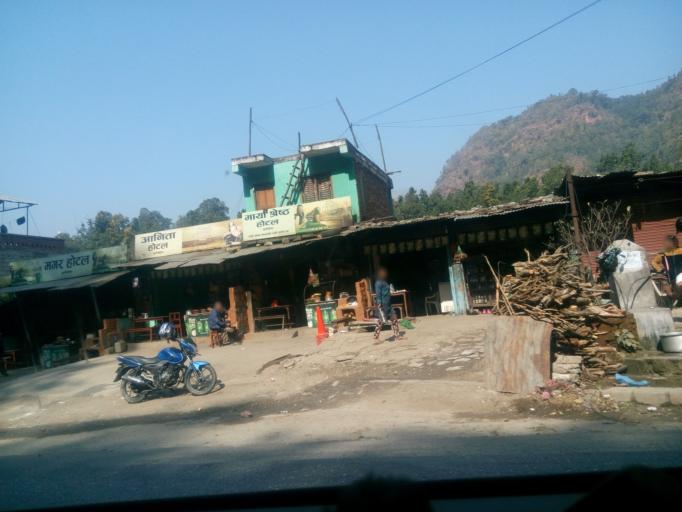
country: NP
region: Central Region
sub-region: Narayani Zone
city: Hitura
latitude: 27.8021
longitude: 84.8452
